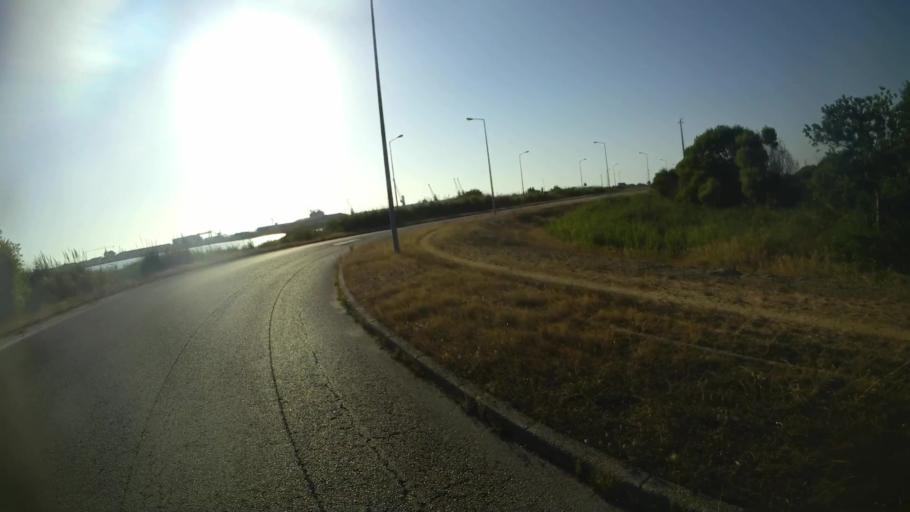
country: PT
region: Aveiro
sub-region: Aveiro
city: Aveiro
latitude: 40.6356
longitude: -8.6735
